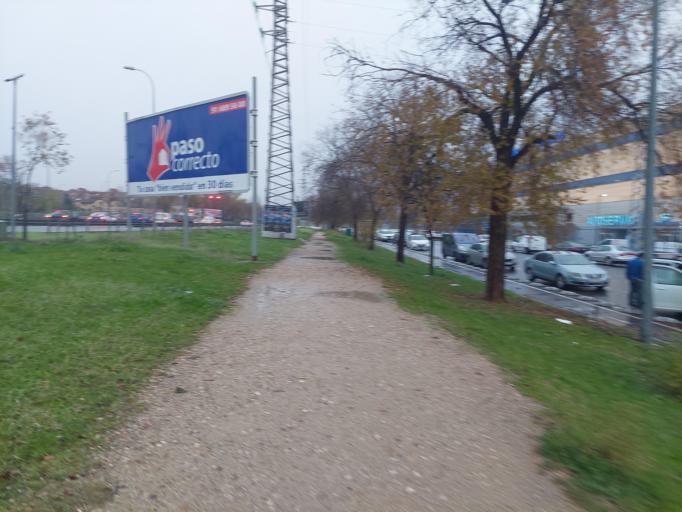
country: ES
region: Madrid
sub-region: Provincia de Madrid
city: Leganes
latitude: 40.3228
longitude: -3.7553
